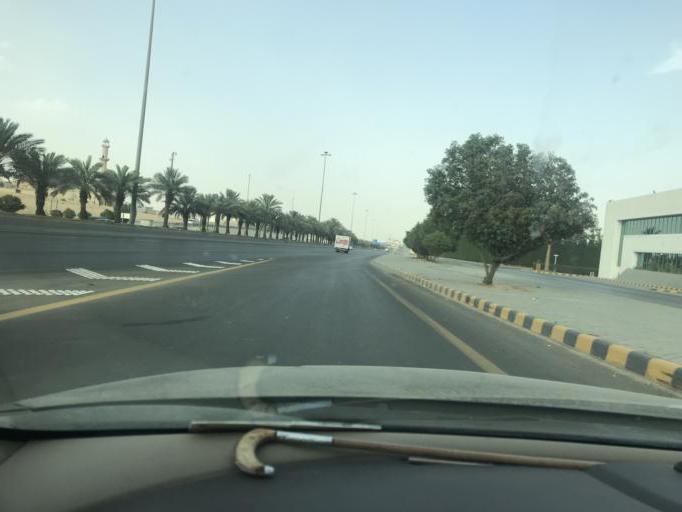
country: SA
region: Ar Riyad
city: Riyadh
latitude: 24.7857
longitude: 46.7069
